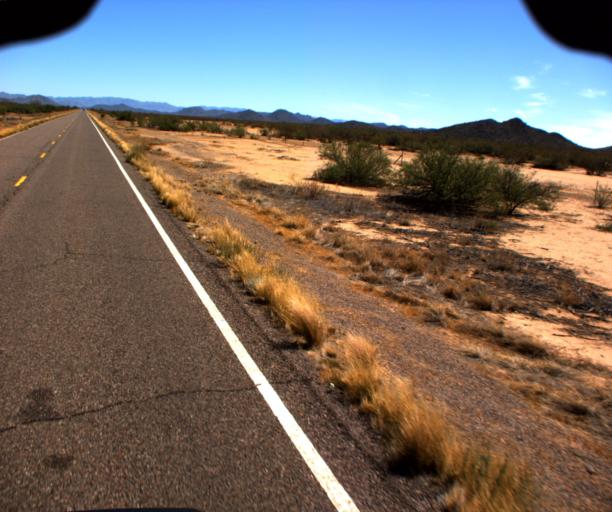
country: US
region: Arizona
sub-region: Yavapai County
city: Congress
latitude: 34.0124
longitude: -113.1062
